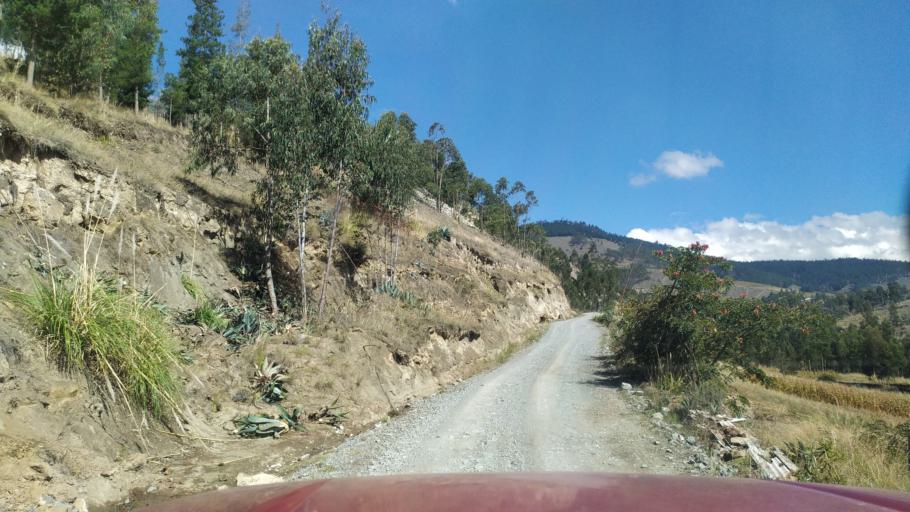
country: EC
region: Chimborazo
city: Riobamba
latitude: -1.6811
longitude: -78.6923
